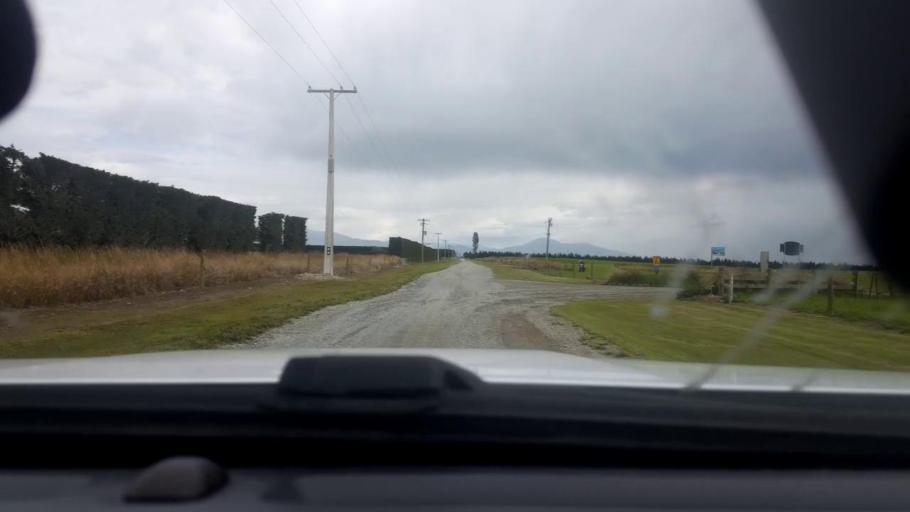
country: NZ
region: Canterbury
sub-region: Timaru District
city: Timaru
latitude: -44.1731
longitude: 171.4172
